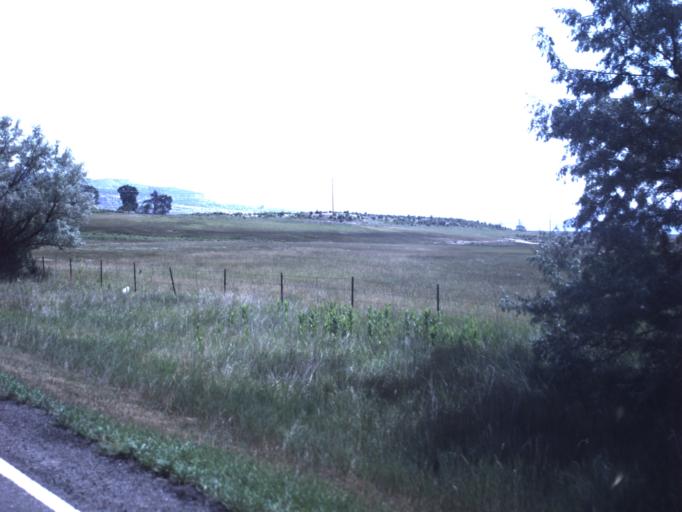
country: US
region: Utah
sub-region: Daggett County
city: Manila
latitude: 40.9963
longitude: -109.6797
